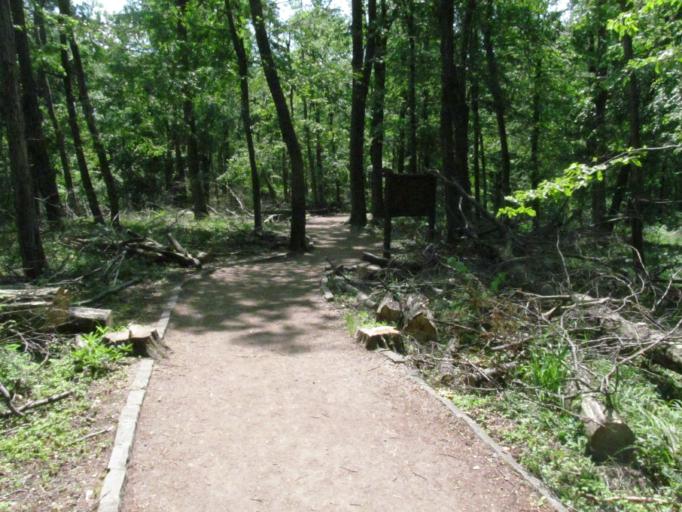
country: HU
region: Pest
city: Pilisszentkereszt
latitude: 47.7226
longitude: 18.8913
